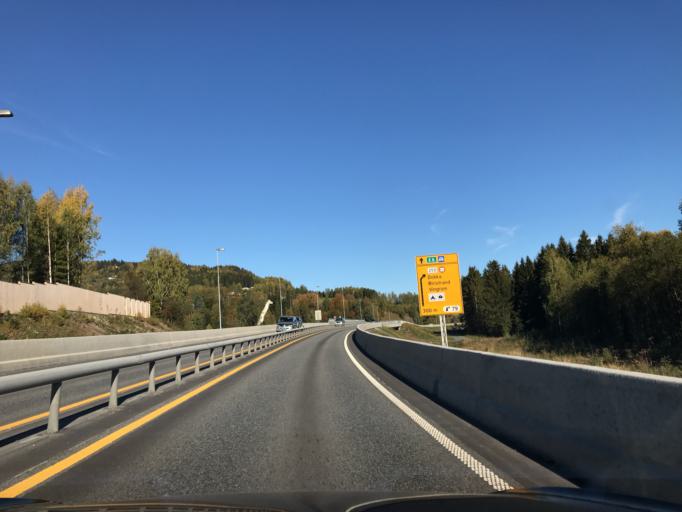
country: NO
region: Oppland
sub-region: Lillehammer
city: Lillehammer
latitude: 61.0435
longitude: 10.4345
